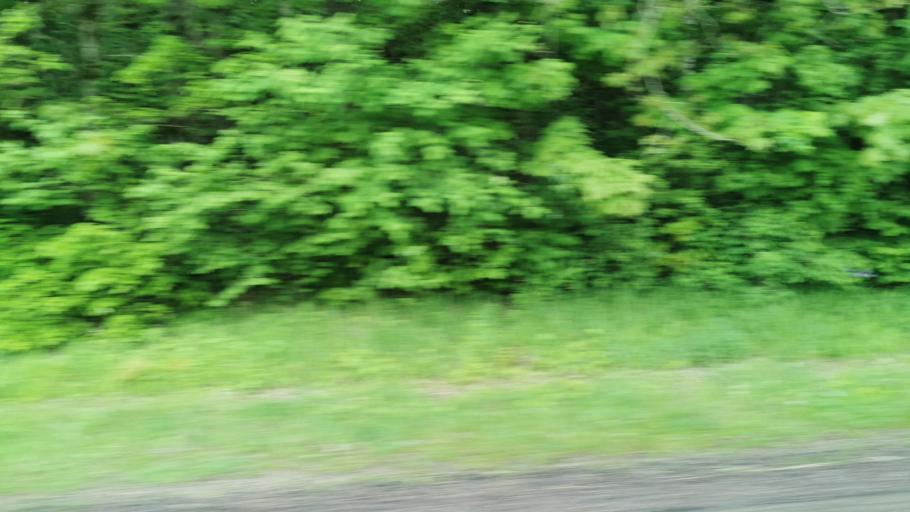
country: EE
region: Laeaene-Virumaa
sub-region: Rakvere linn
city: Rakvere
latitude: 59.2716
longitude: 26.3542
